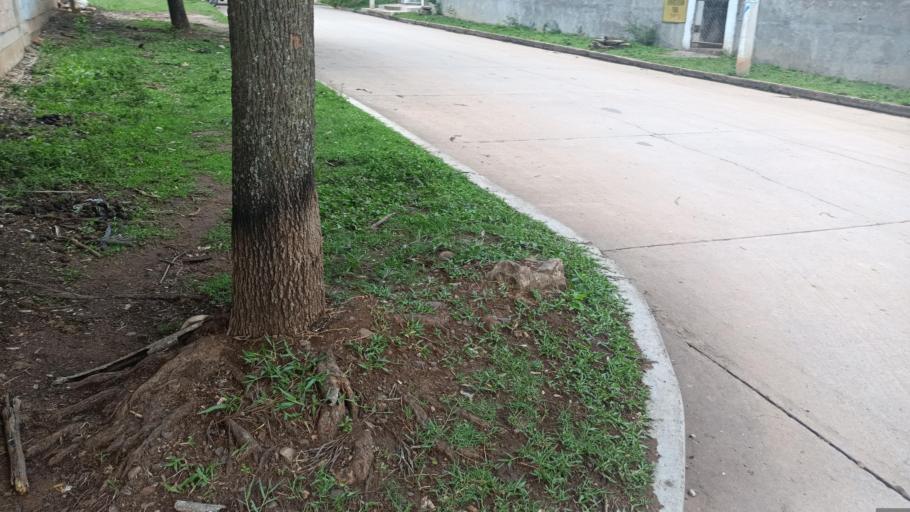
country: BO
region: Tarija
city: Entre Rios
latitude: -21.5304
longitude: -64.1729
